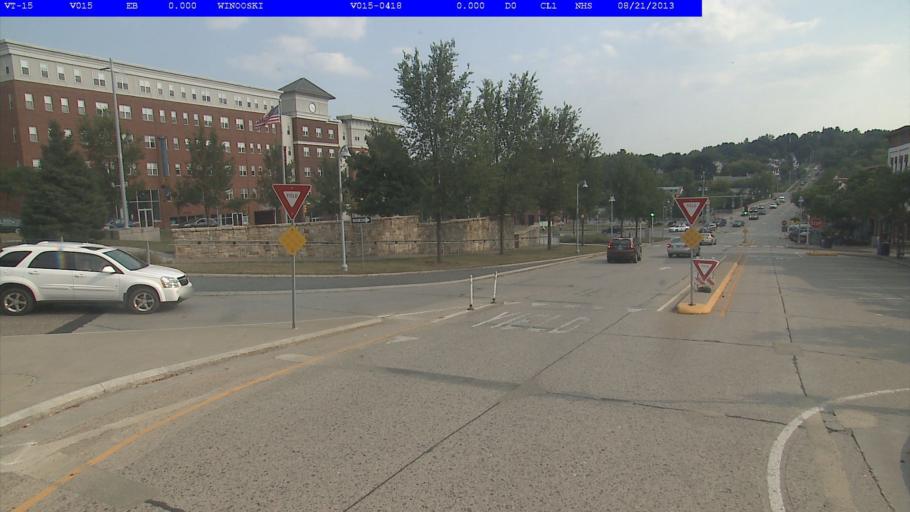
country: US
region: Vermont
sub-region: Chittenden County
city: Winooski
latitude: 44.4913
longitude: -73.1865
